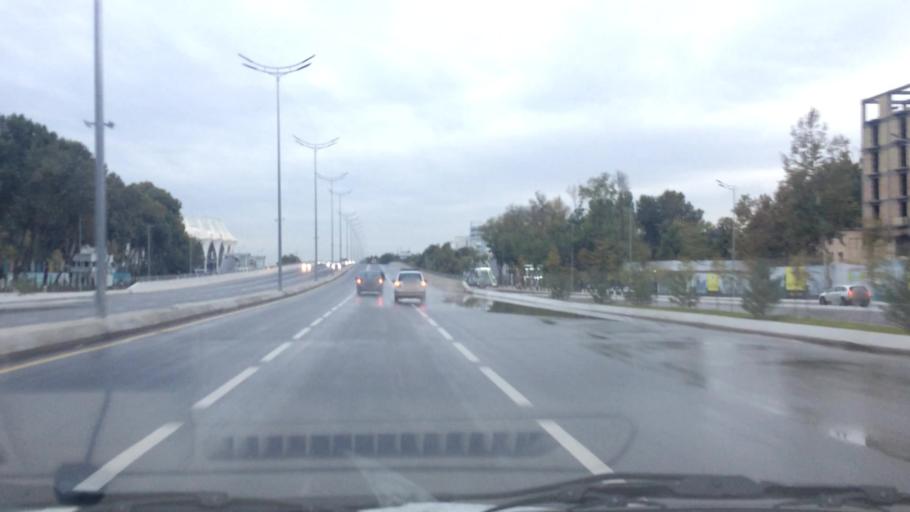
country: UZ
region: Toshkent Shahri
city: Tashkent
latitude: 41.2848
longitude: 69.2151
